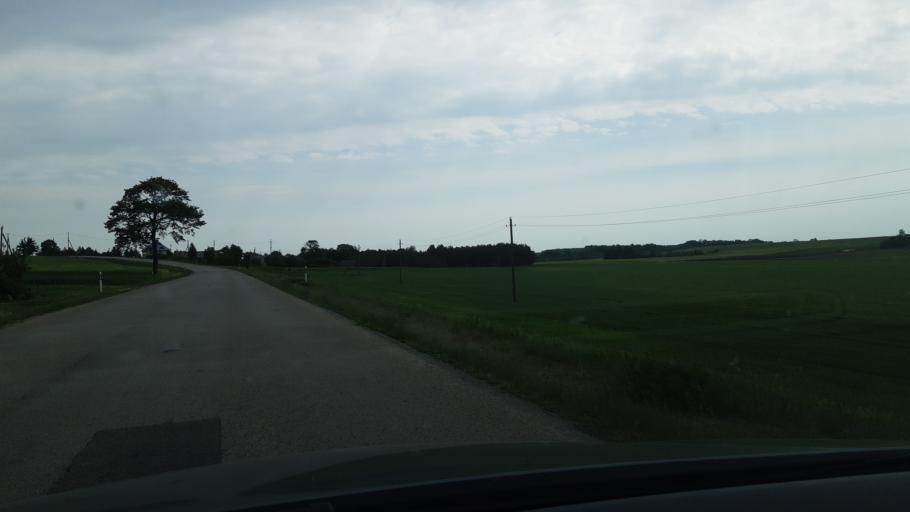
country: LT
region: Kauno apskritis
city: Kedainiai
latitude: 55.1736
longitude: 23.8645
